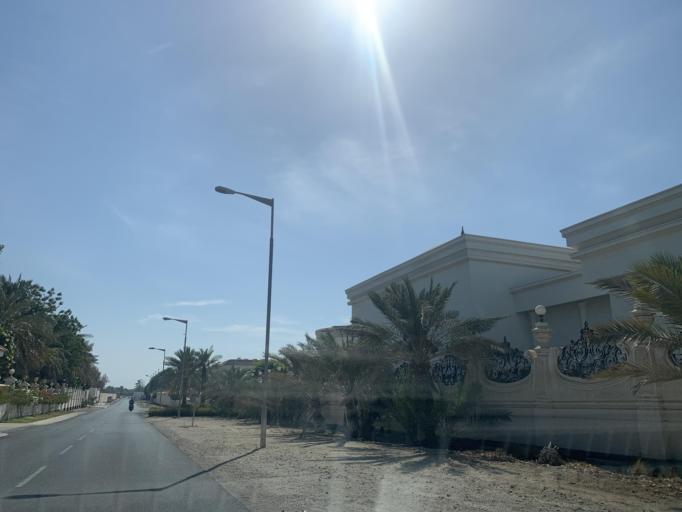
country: BH
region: Northern
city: Madinat `Isa
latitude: 26.1929
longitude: 50.4744
